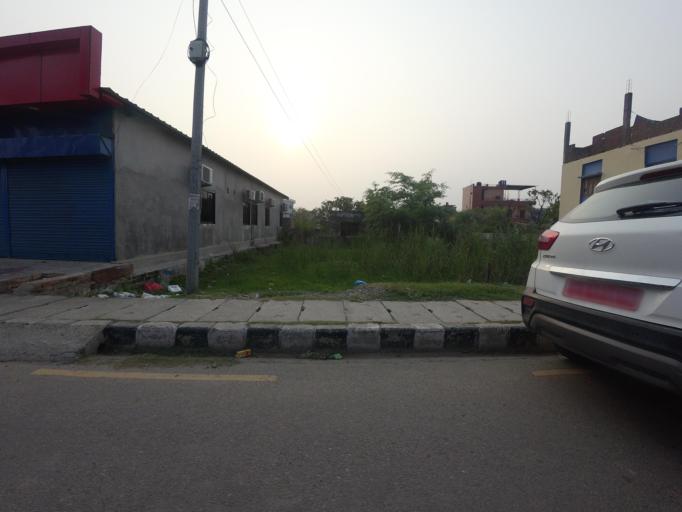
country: NP
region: Western Region
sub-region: Lumbini Zone
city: Bhairahawa
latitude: 27.5147
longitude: 83.4486
